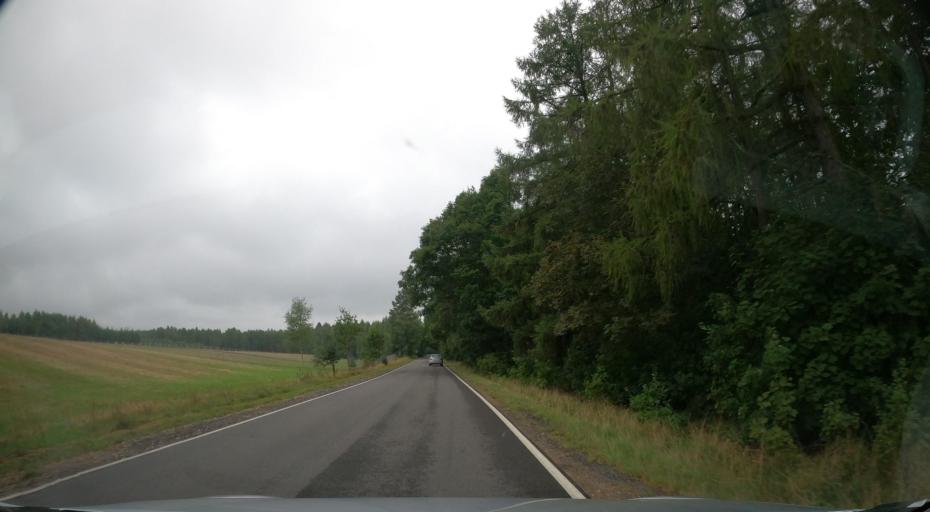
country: PL
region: Pomeranian Voivodeship
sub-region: Powiat wejherowski
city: Linia
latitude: 54.4935
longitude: 17.8416
